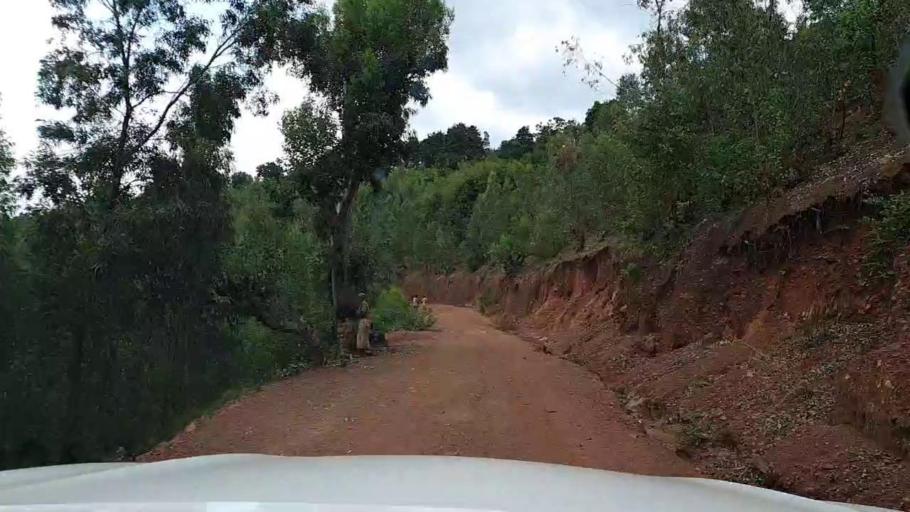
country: RW
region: Southern Province
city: Butare
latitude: -2.7549
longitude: 29.7511
